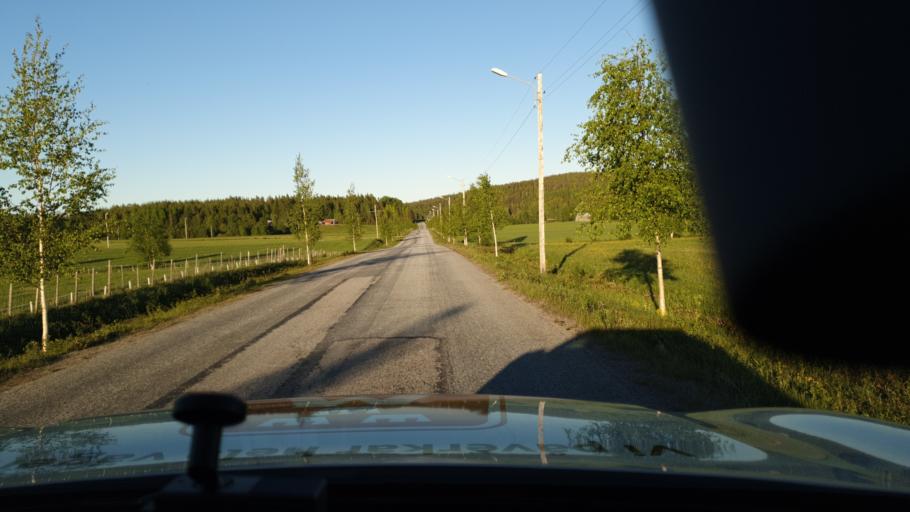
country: SE
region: Vaesterbotten
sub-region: Umea Kommun
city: Roback
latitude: 64.0119
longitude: 20.1463
